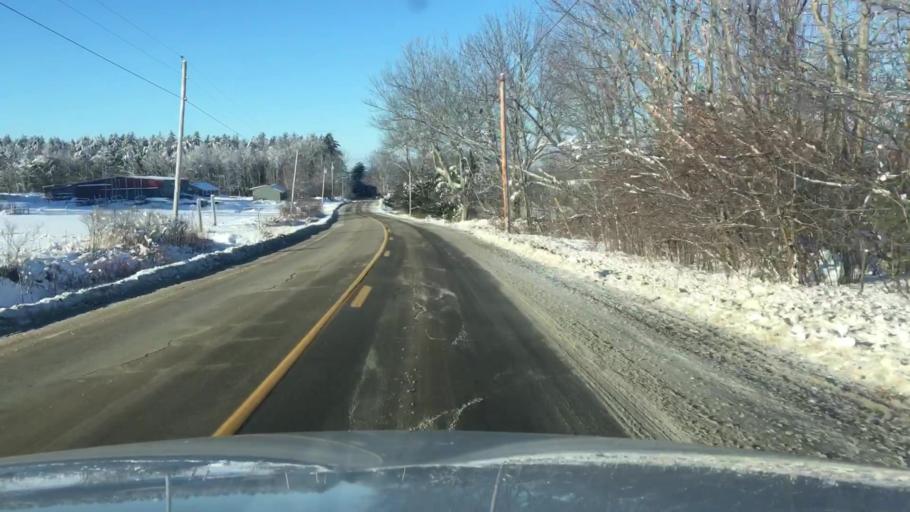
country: US
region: Maine
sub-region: Kennebec County
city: Readfield
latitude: 44.4316
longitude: -69.9519
